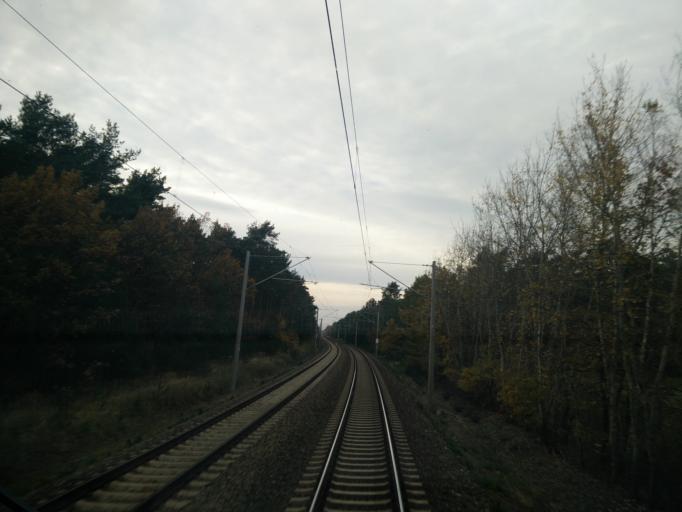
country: DE
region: Brandenburg
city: Luebben
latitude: 51.9501
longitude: 13.8595
